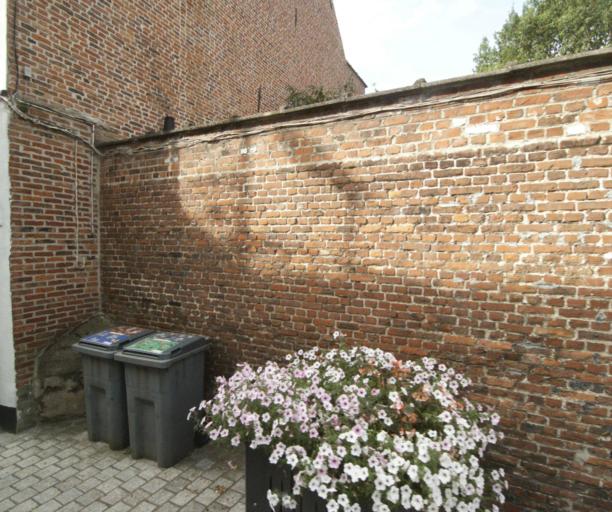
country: FR
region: Nord-Pas-de-Calais
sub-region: Departement du Nord
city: Linselles
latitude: 50.7378
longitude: 3.0799
